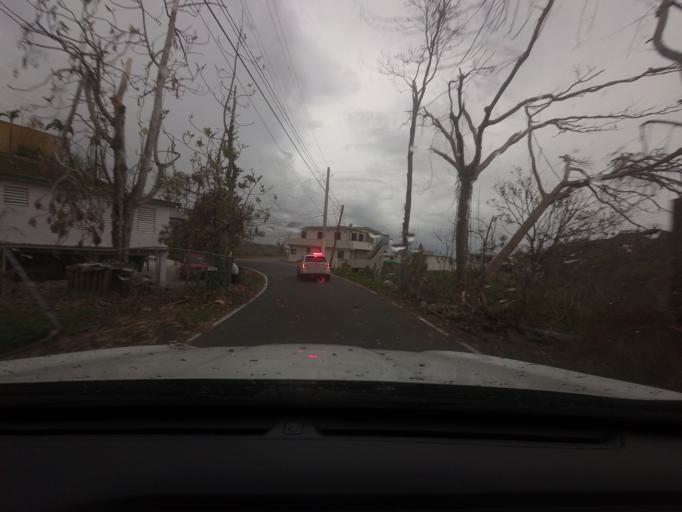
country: PR
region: Ciales
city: Ciales
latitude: 18.2789
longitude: -66.4792
